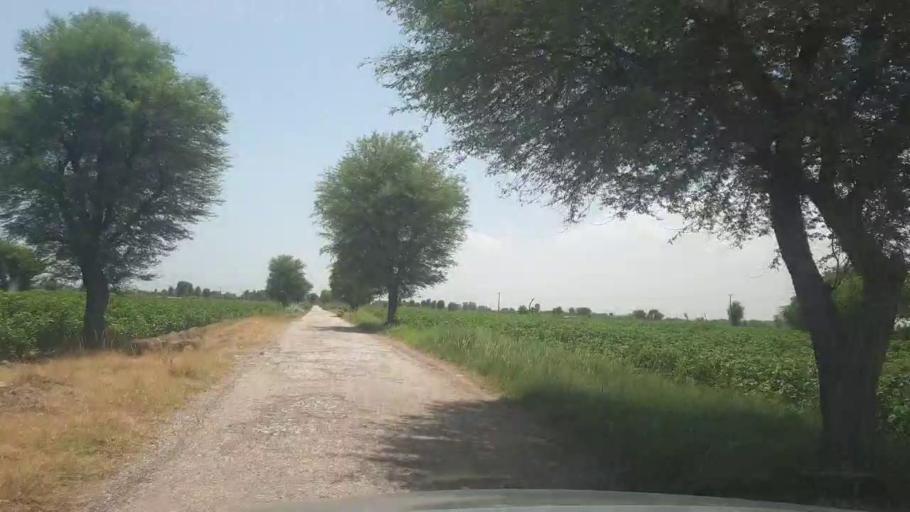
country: PK
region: Sindh
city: Kot Diji
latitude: 27.2724
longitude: 69.0213
